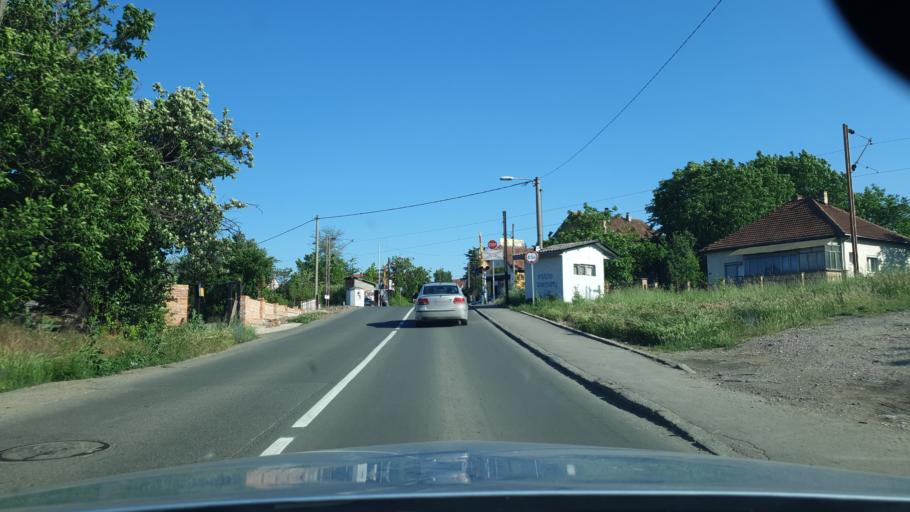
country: RS
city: Ostruznica
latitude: 44.7213
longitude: 20.3668
